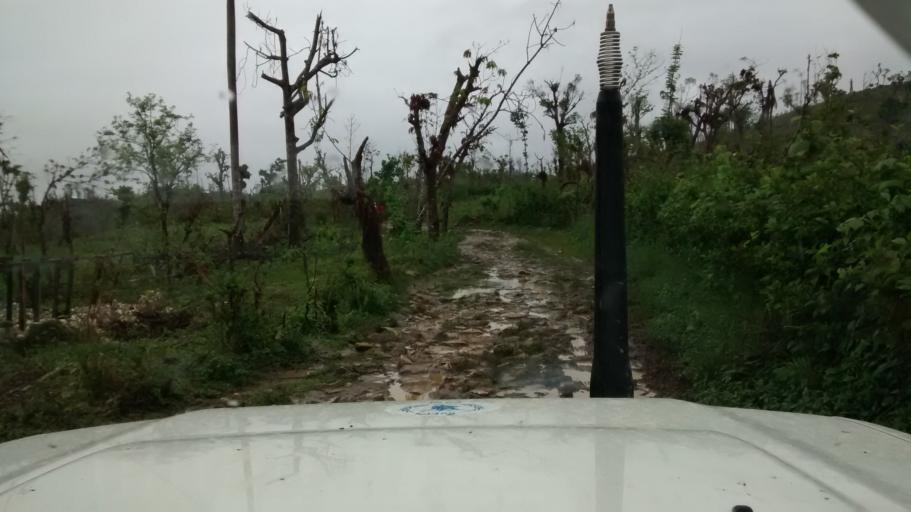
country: HT
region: Grandans
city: Moron
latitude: 18.5257
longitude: -74.1531
